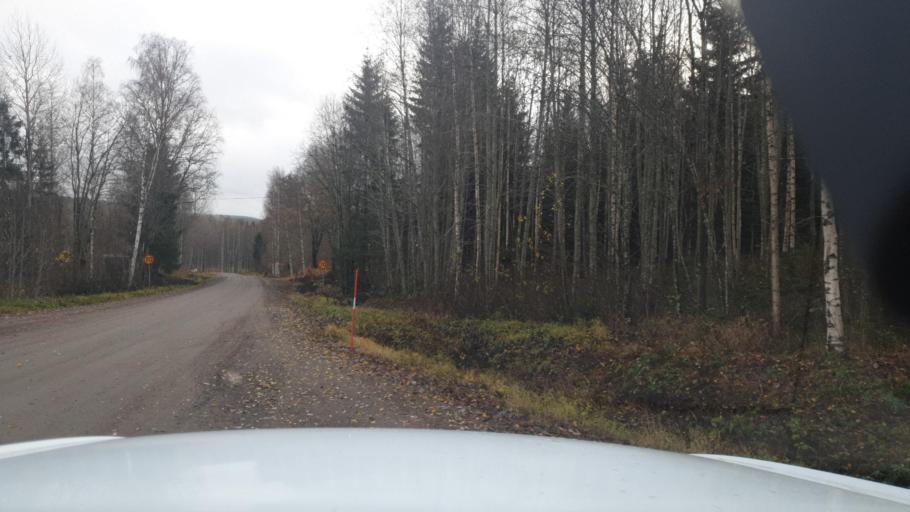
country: SE
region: Vaermland
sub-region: Eda Kommun
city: Charlottenberg
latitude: 60.0927
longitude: 12.4956
